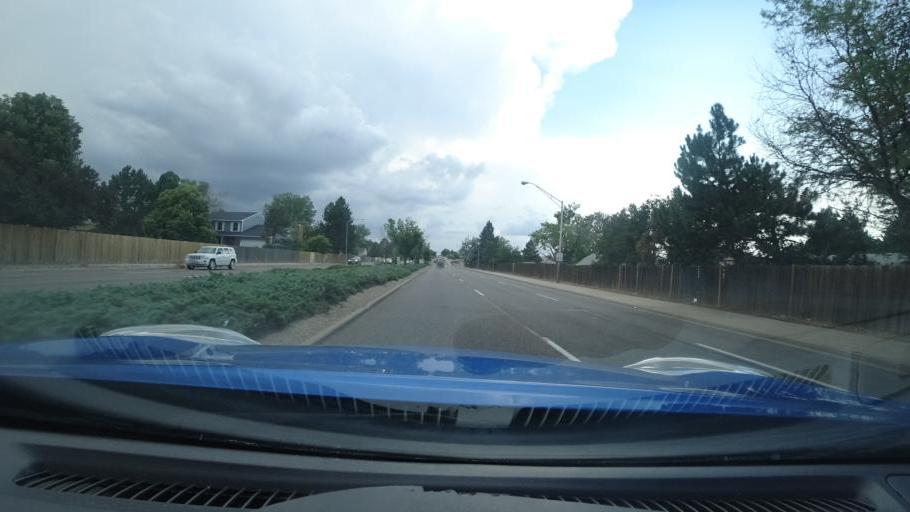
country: US
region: Colorado
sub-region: Adams County
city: Aurora
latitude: 39.6967
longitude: -104.8033
